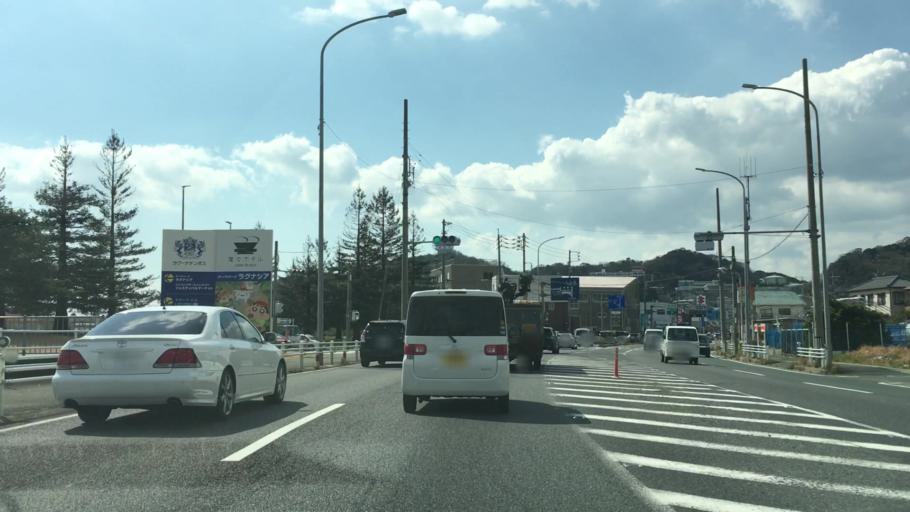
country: JP
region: Aichi
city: Gamagori
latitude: 34.8111
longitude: 137.2744
